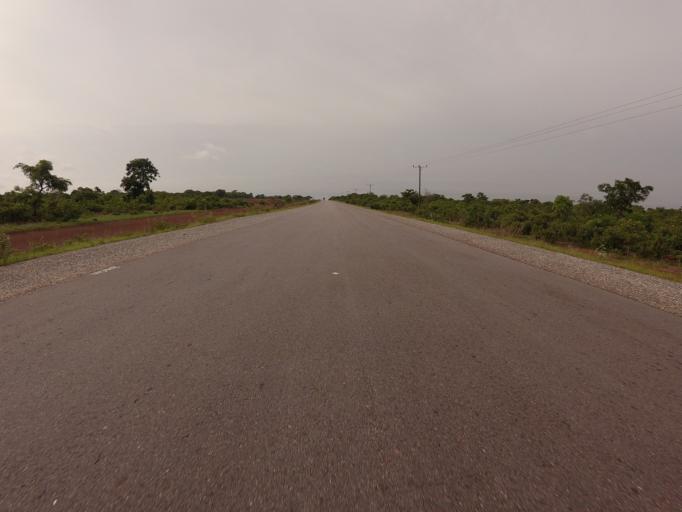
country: GH
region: Northern
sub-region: Yendi
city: Yendi
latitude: 9.6181
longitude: -0.0496
